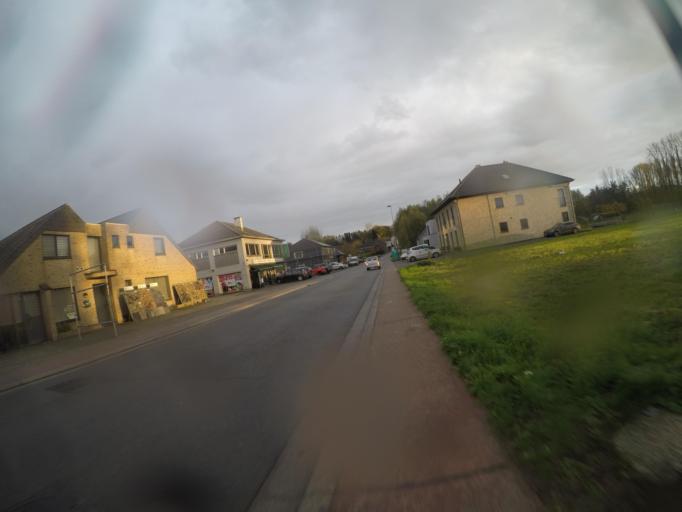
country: BE
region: Flanders
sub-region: Provincie Vlaams-Brabant
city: Ternat
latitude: 50.8521
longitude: 4.1339
